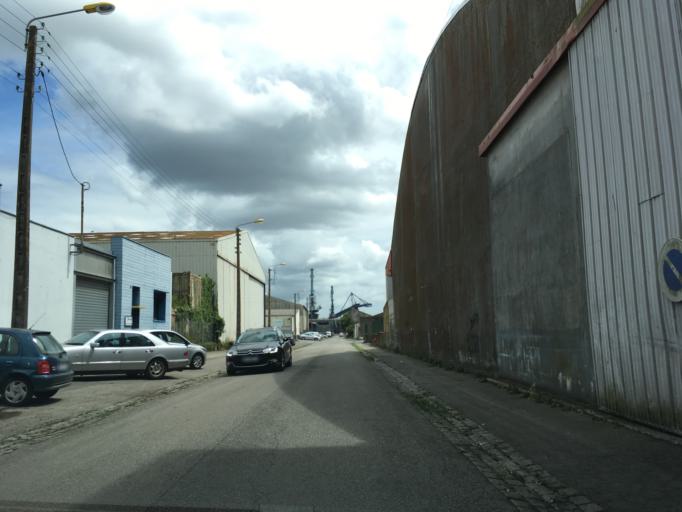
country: FR
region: Brittany
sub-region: Departement du Morbihan
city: Lorient
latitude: 47.7342
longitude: -3.3636
